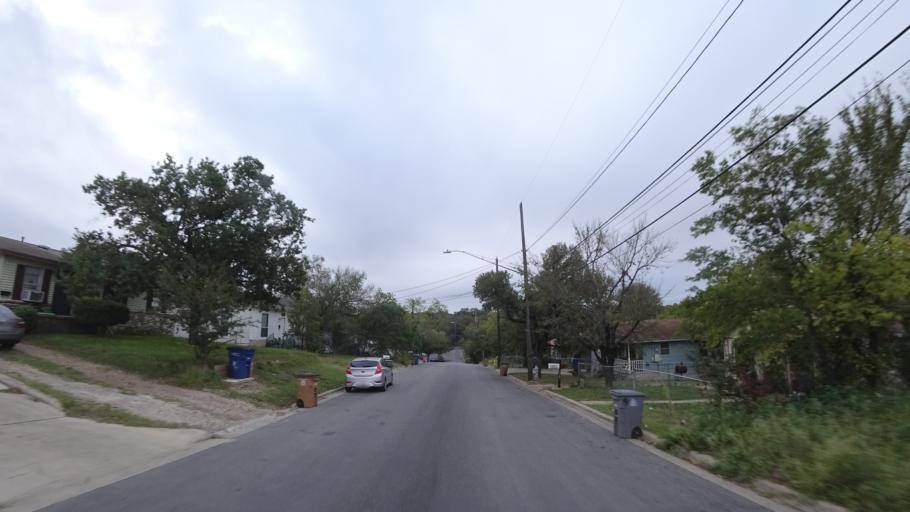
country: US
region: Texas
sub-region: Travis County
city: Austin
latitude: 30.2797
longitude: -97.6949
